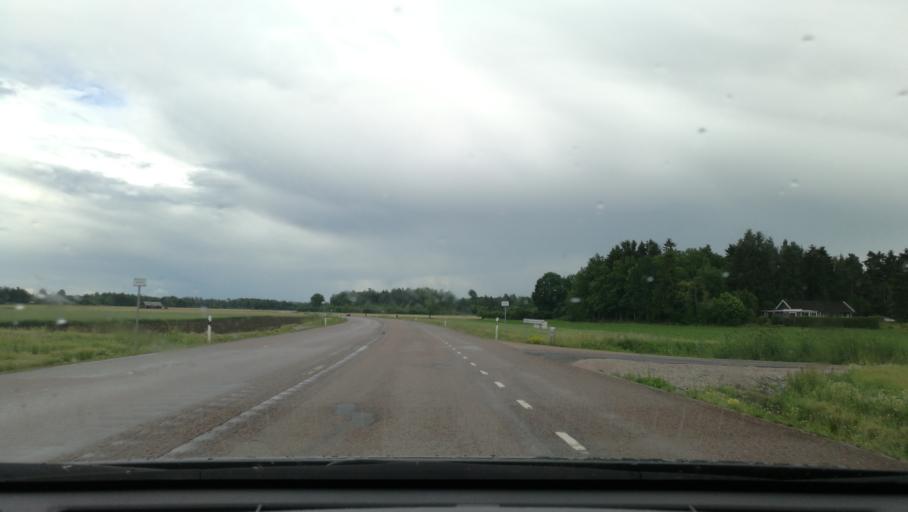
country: SE
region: Vaestmanland
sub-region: Kopings Kommun
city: Koping
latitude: 59.4603
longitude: 16.0036
